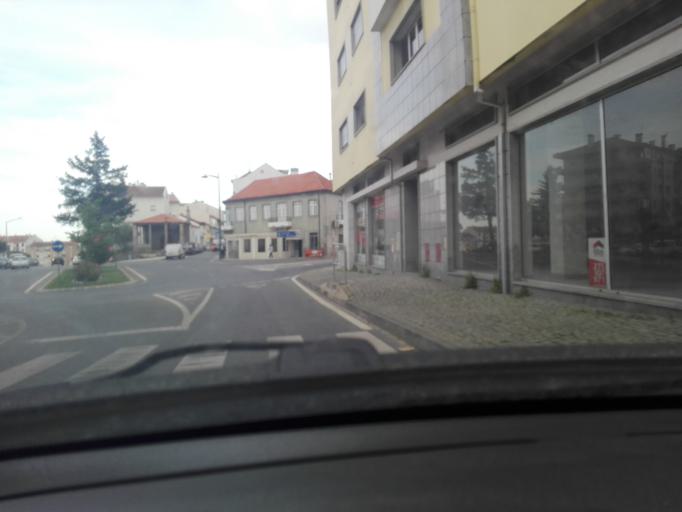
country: PT
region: Castelo Branco
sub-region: Concelho do Fundao
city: Fundao
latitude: 40.1354
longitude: -7.5048
